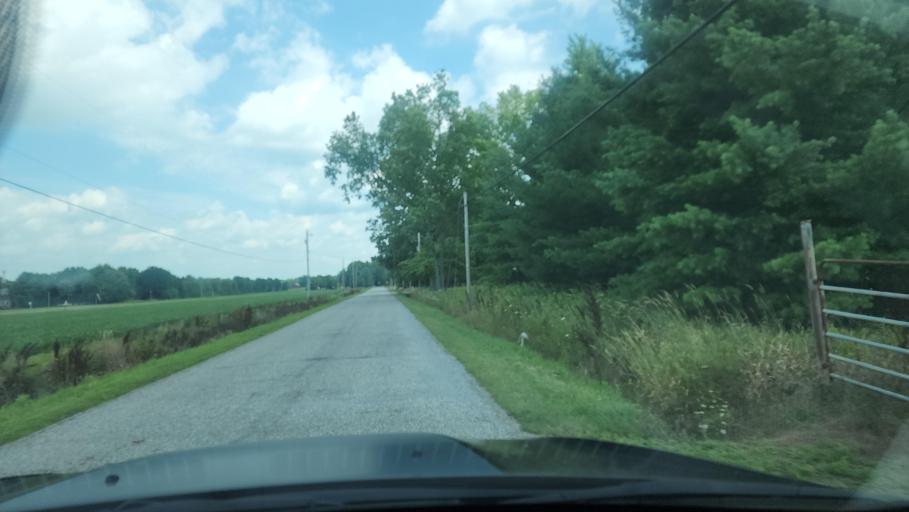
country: US
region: Ohio
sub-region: Trumbull County
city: Leavittsburg
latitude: 41.2685
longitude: -80.9249
